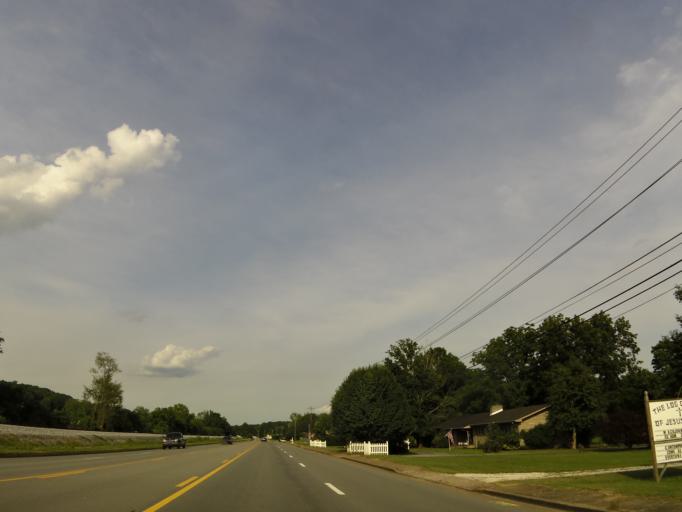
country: US
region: Tennessee
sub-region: Humphreys County
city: Waverly
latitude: 36.0862
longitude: -87.7518
